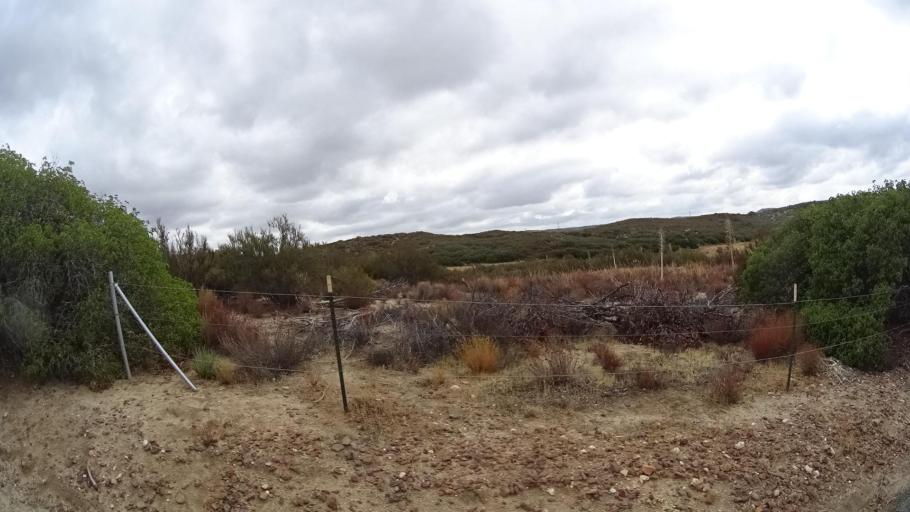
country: US
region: California
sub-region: San Diego County
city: Pine Valley
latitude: 32.7314
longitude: -116.4570
